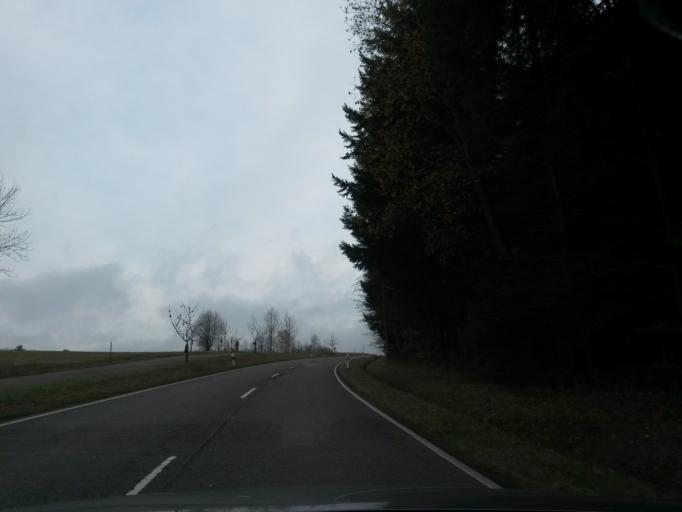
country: DE
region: Baden-Wuerttemberg
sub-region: Karlsruhe Region
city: Lossburg
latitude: 48.3998
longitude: 8.4551
